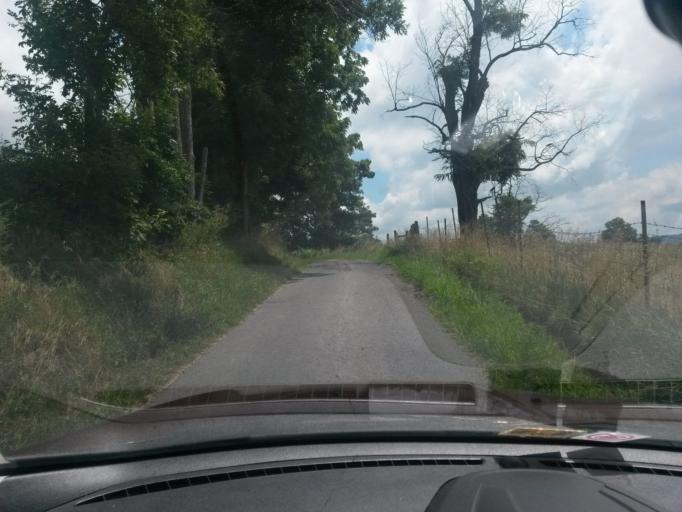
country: US
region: West Virginia
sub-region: Monroe County
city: Union
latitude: 37.5579
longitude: -80.5140
